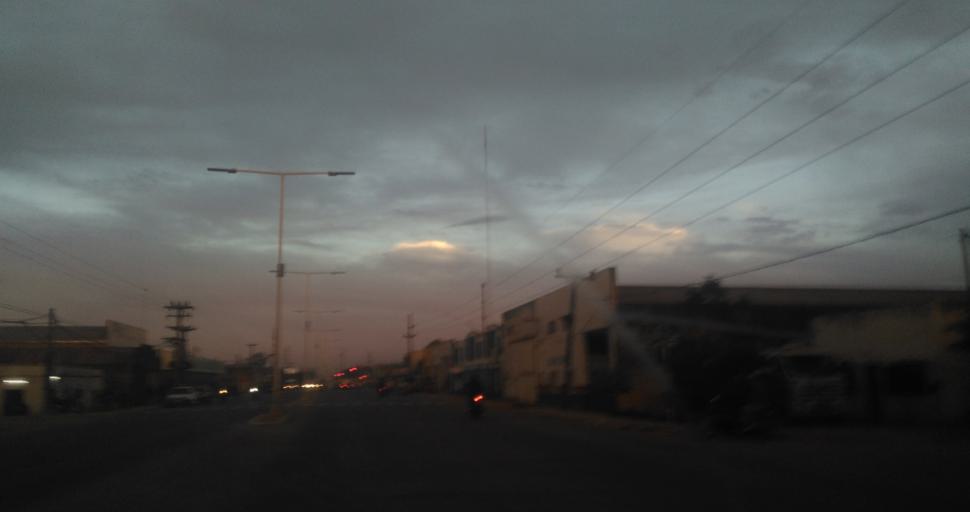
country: AR
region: Chaco
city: Fontana
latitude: -27.4350
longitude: -59.0191
